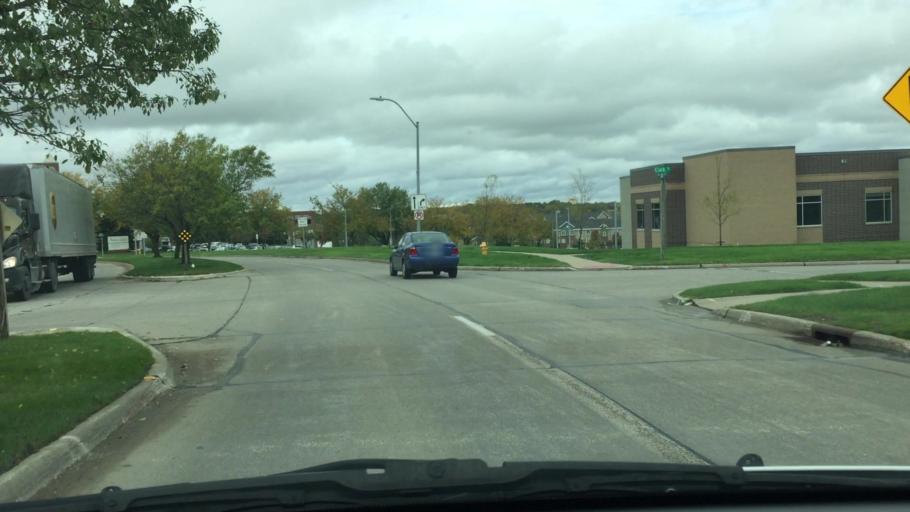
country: US
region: Iowa
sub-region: Polk County
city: Clive
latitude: 41.6028
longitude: -93.7715
